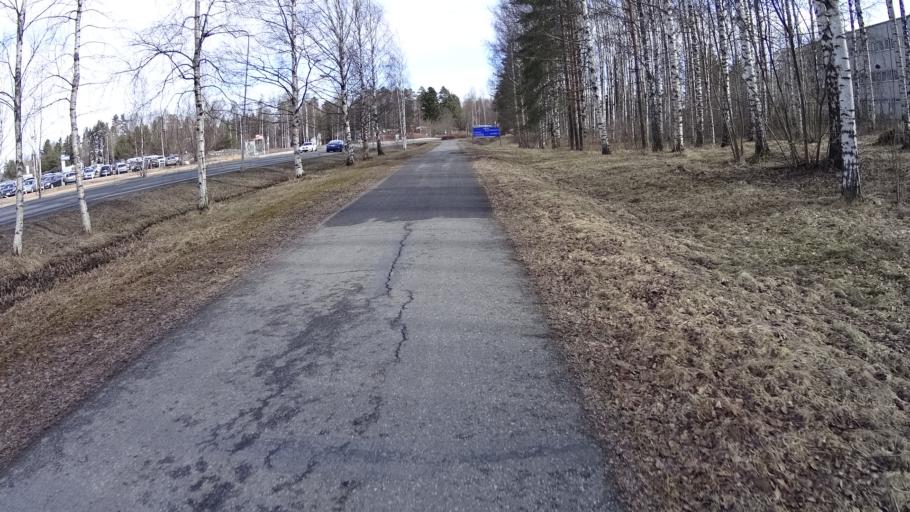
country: FI
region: Uusimaa
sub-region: Helsinki
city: Teekkarikylae
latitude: 60.2643
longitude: 24.8812
